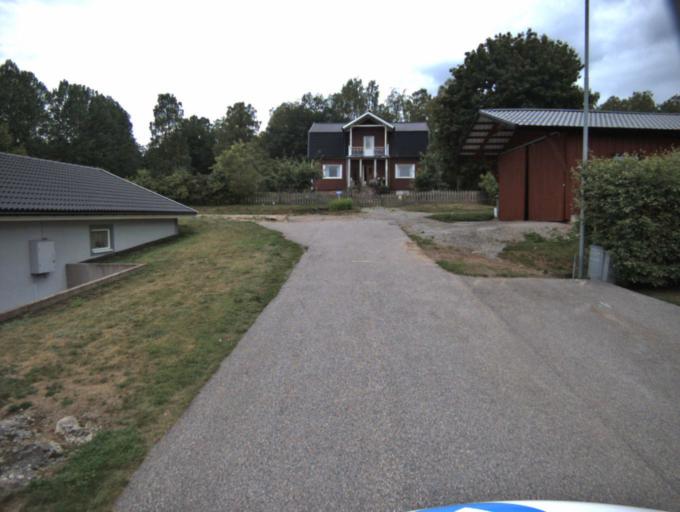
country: SE
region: Vaestra Goetaland
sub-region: Ulricehamns Kommun
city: Ulricehamn
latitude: 57.6701
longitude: 13.3670
